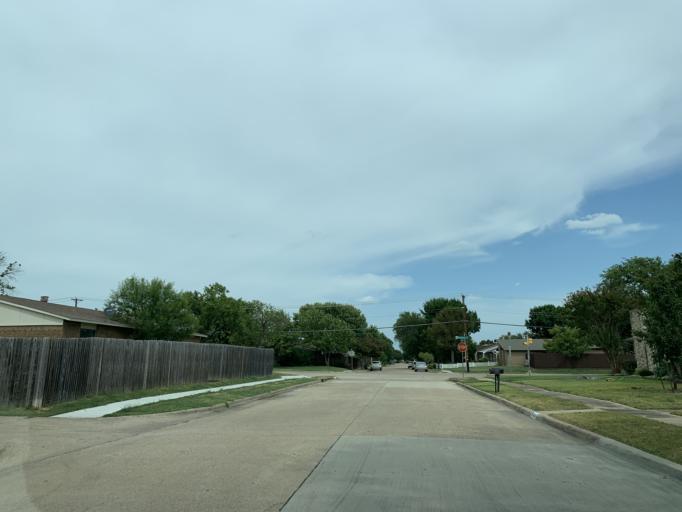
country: US
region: Texas
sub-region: Dallas County
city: Cedar Hill
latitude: 32.6534
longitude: -97.0285
